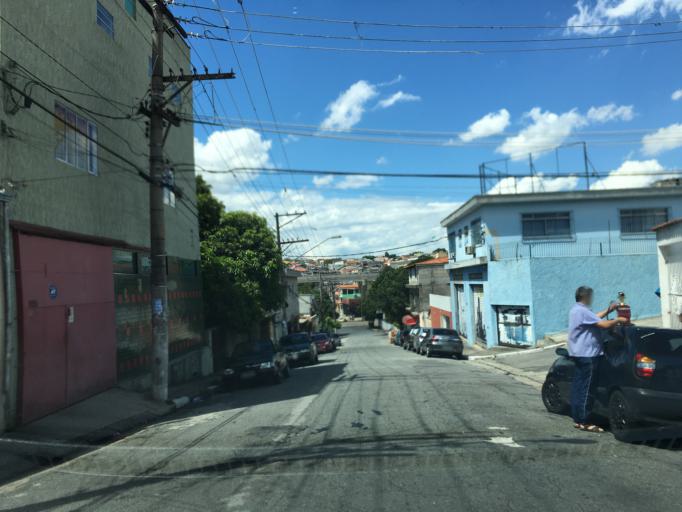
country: BR
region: Sao Paulo
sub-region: Sao Caetano Do Sul
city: Sao Caetano do Sul
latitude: -23.5995
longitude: -46.5342
